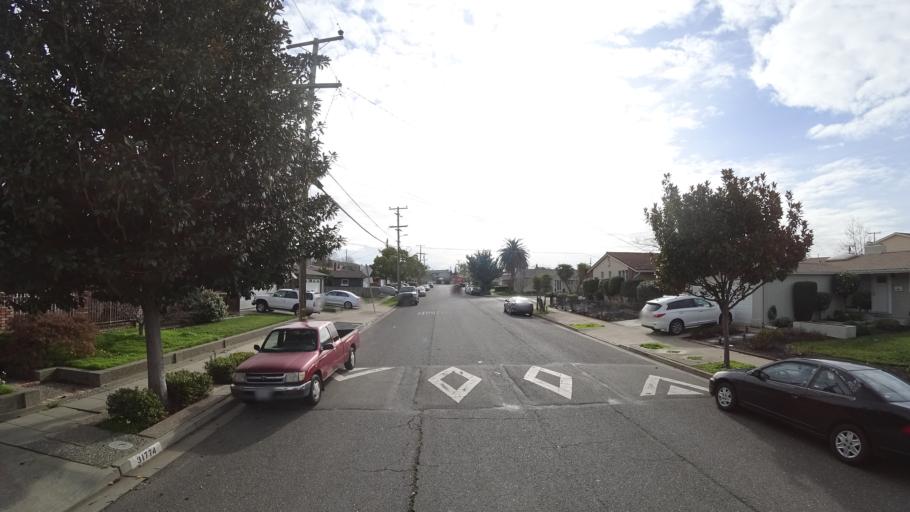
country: US
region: California
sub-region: Alameda County
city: Union City
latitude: 37.6155
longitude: -122.0315
